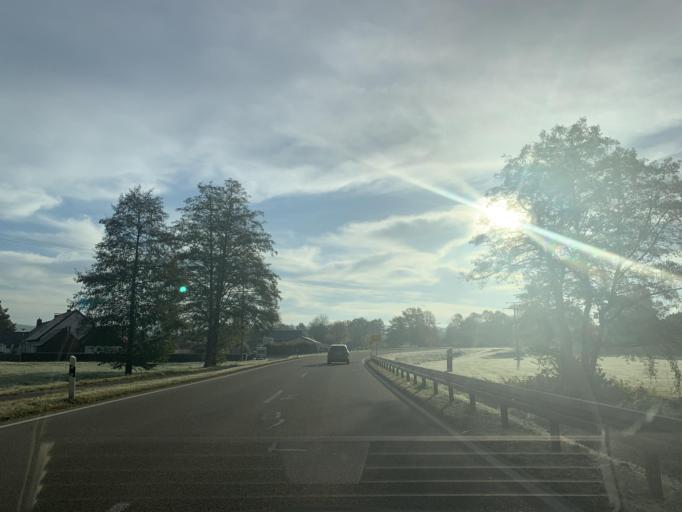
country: DE
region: Bavaria
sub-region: Upper Palatinate
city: Neunburg vorm Wald
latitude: 49.3524
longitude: 12.3804
